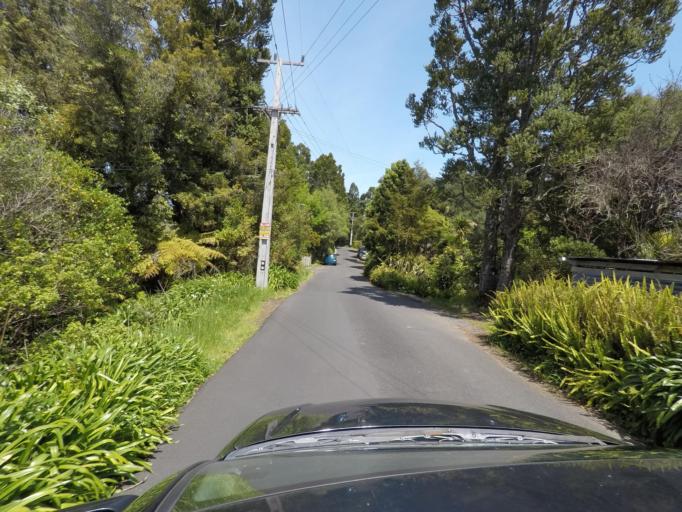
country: NZ
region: Auckland
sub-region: Auckland
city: Titirangi
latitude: -36.9730
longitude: 174.6329
